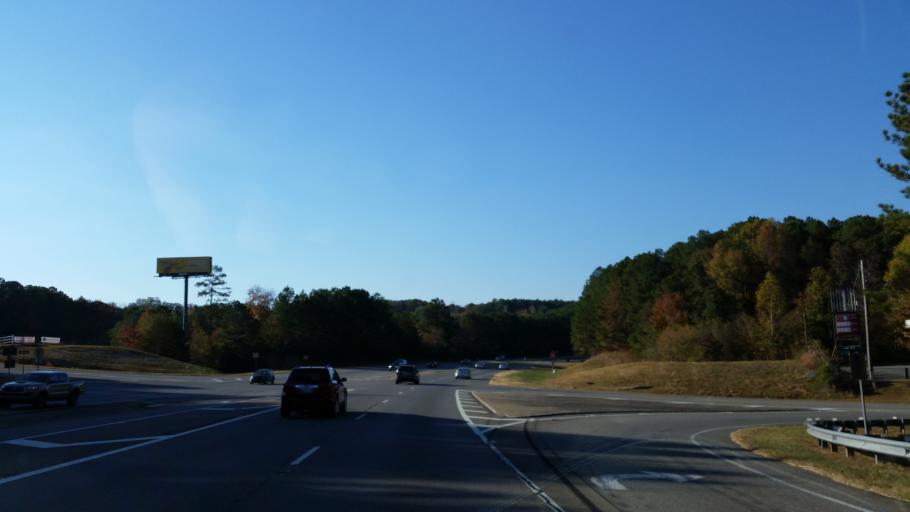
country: US
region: Georgia
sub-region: Pickens County
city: Jasper
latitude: 34.5069
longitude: -84.5148
